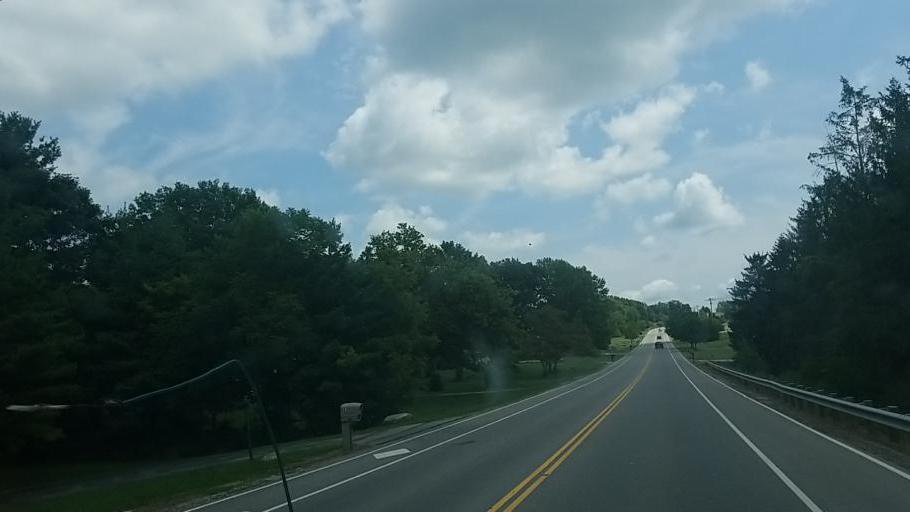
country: US
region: Ohio
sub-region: Fairfield County
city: Pickerington
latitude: 39.8837
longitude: -82.7473
